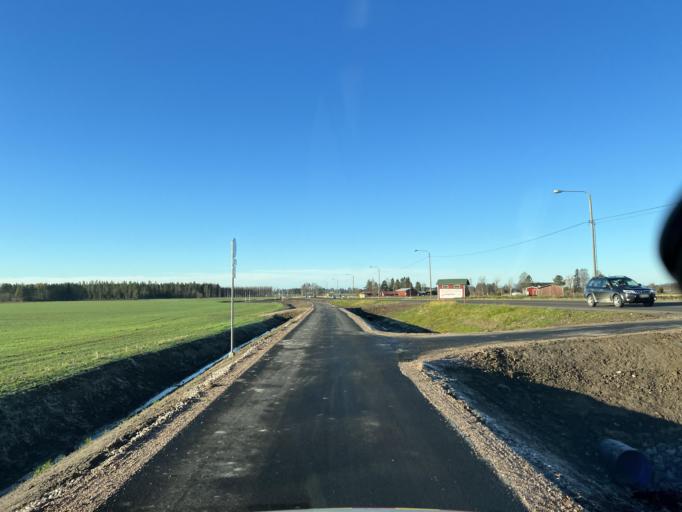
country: FI
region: Northern Ostrobothnia
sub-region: Nivala-Haapajaervi
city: Nivala
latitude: 63.9510
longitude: 24.9059
